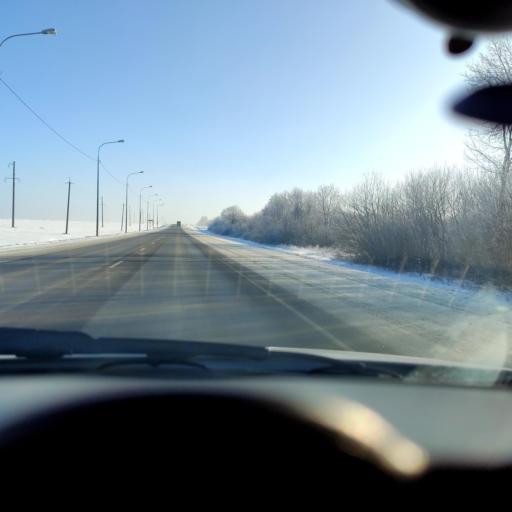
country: RU
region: Kursk
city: Tim
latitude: 51.6547
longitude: 36.9208
